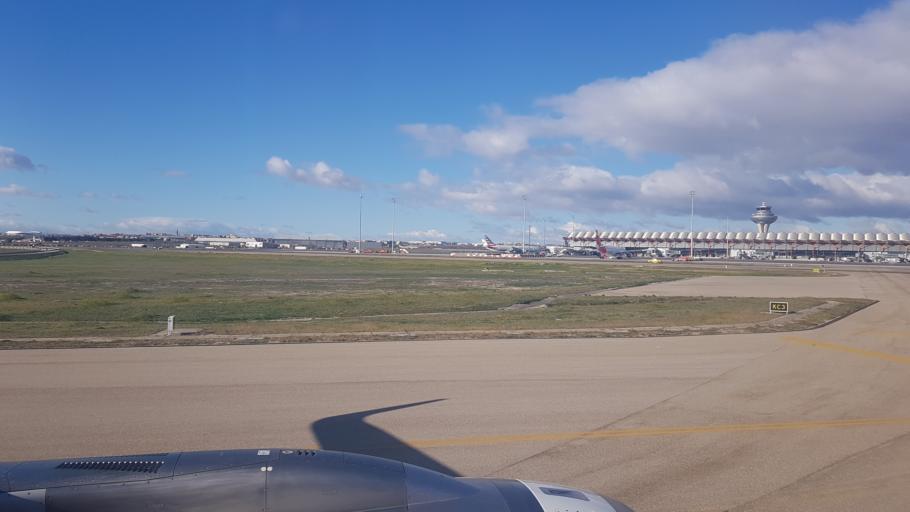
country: ES
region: Madrid
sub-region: Provincia de Madrid
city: Barajas de Madrid
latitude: 40.4925
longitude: -3.5585
